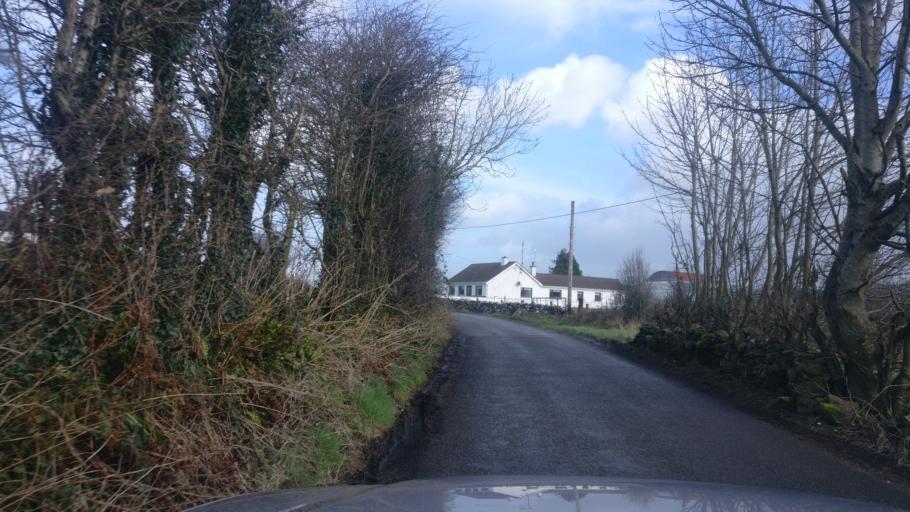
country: IE
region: Connaught
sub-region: County Galway
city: Loughrea
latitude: 53.2605
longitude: -8.5810
